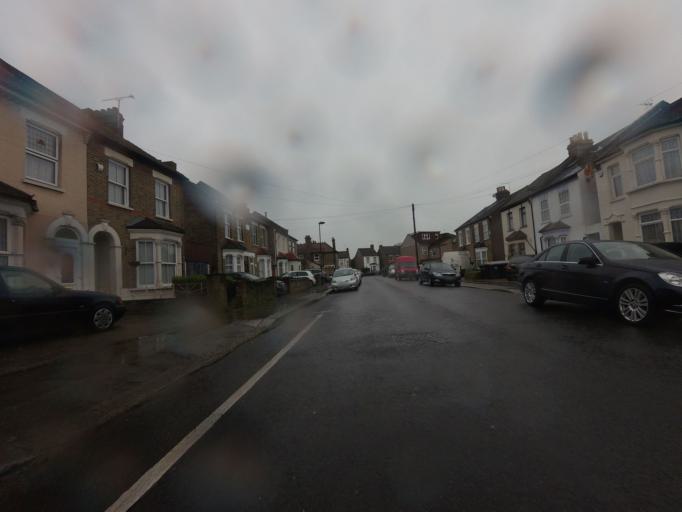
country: GB
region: England
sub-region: Hertfordshire
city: Waltham Cross
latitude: 51.6747
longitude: -0.0321
